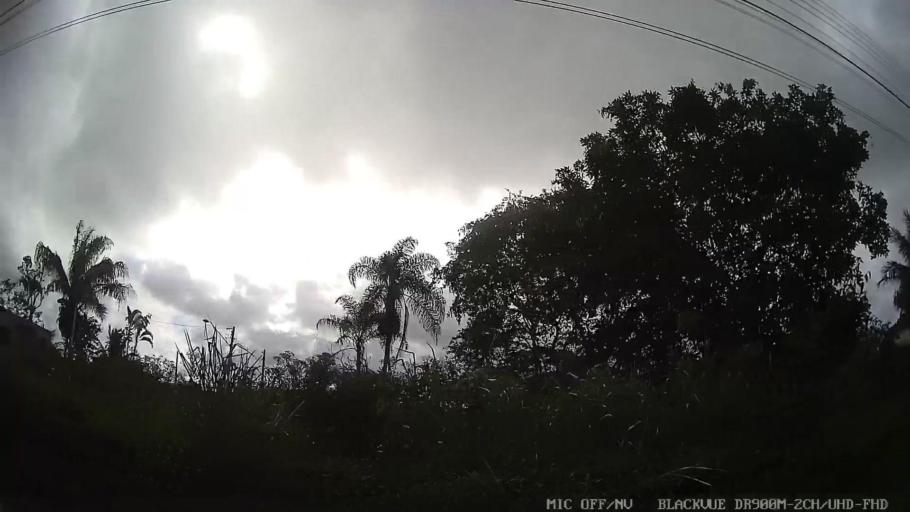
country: BR
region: Sao Paulo
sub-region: Itanhaem
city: Itanhaem
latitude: -24.2238
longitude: -46.9013
